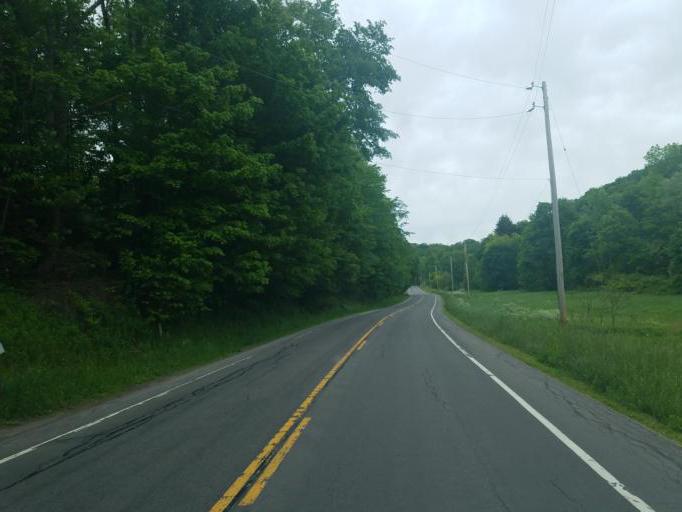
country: US
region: New York
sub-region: Herkimer County
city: Frankfort
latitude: 42.9764
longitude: -75.0957
